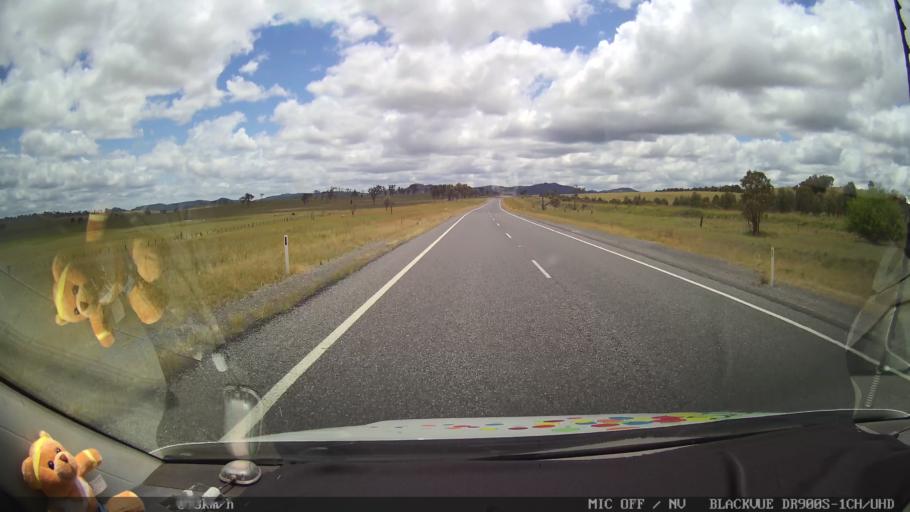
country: AU
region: New South Wales
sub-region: Glen Innes Severn
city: Glen Innes
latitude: -29.4004
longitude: 151.8746
